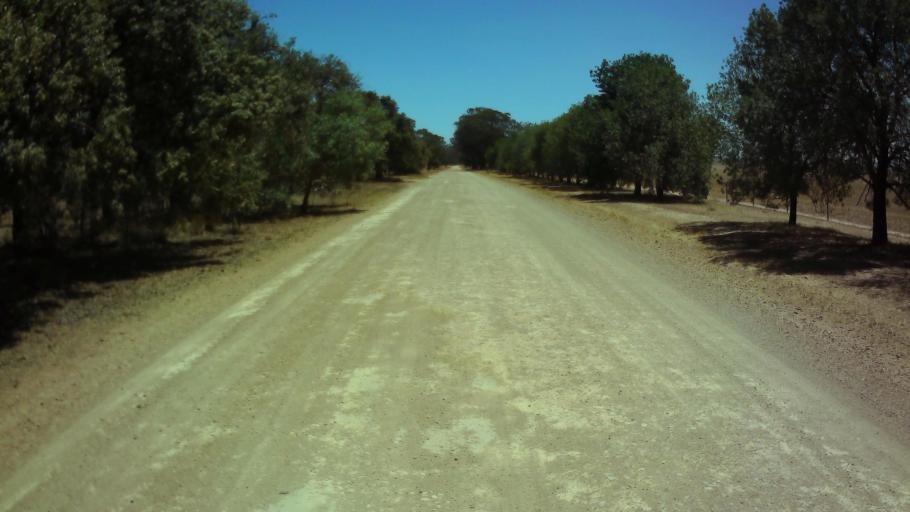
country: AU
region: New South Wales
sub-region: Weddin
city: Grenfell
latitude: -34.0124
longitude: 148.1808
